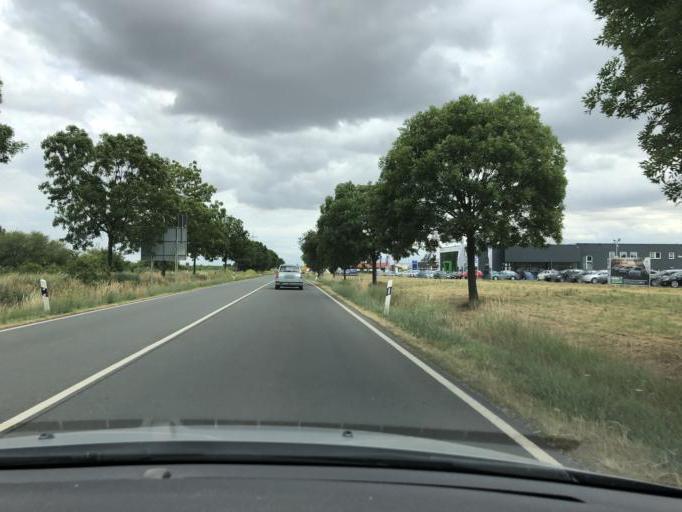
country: DE
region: Saxony-Anhalt
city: Erdeborn
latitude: 51.5083
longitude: 11.5863
